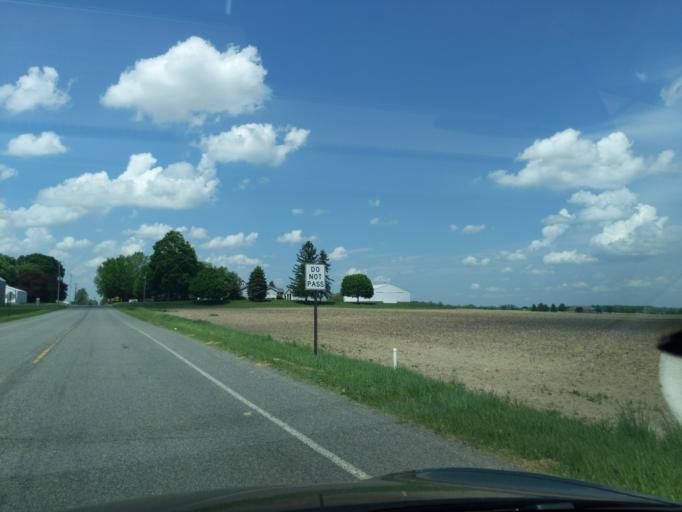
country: US
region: Michigan
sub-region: Ingham County
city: Mason
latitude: 42.6369
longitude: -84.4330
